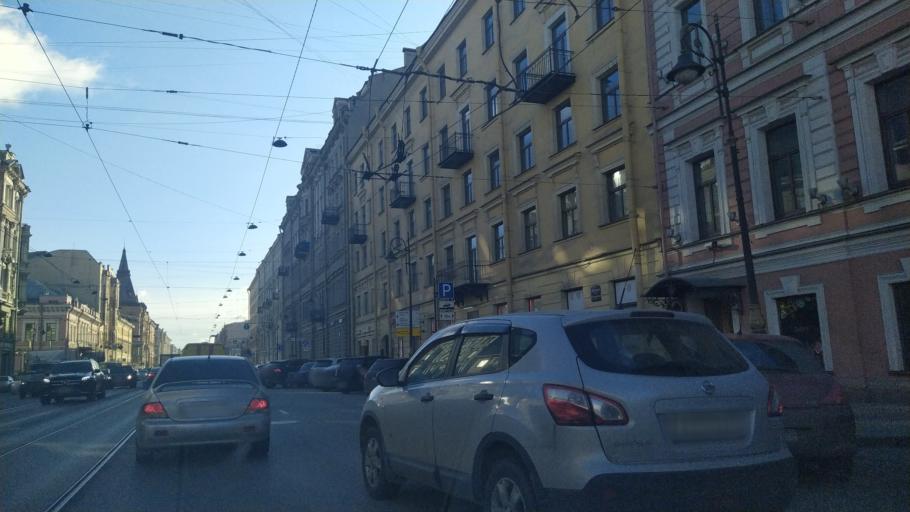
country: RU
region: St.-Petersburg
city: Centralniy
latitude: 59.9463
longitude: 30.3487
